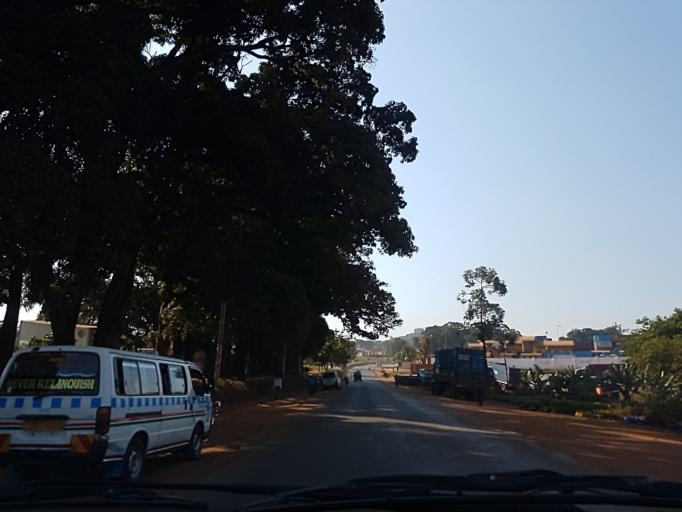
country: UG
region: Central Region
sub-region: Wakiso District
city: Kireka
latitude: 0.3343
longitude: 32.6174
